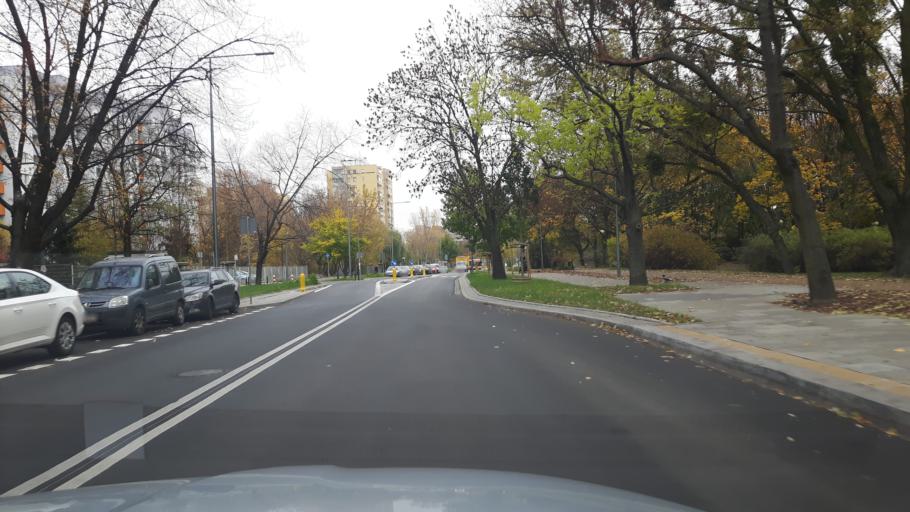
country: PL
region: Masovian Voivodeship
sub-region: Warszawa
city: Targowek
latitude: 52.2743
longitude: 21.0500
